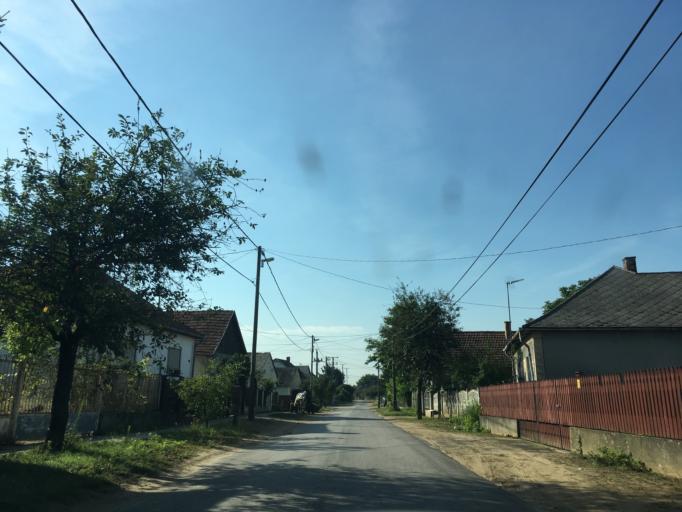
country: HU
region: Szabolcs-Szatmar-Bereg
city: Nyirbeltek
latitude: 47.6932
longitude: 22.1302
